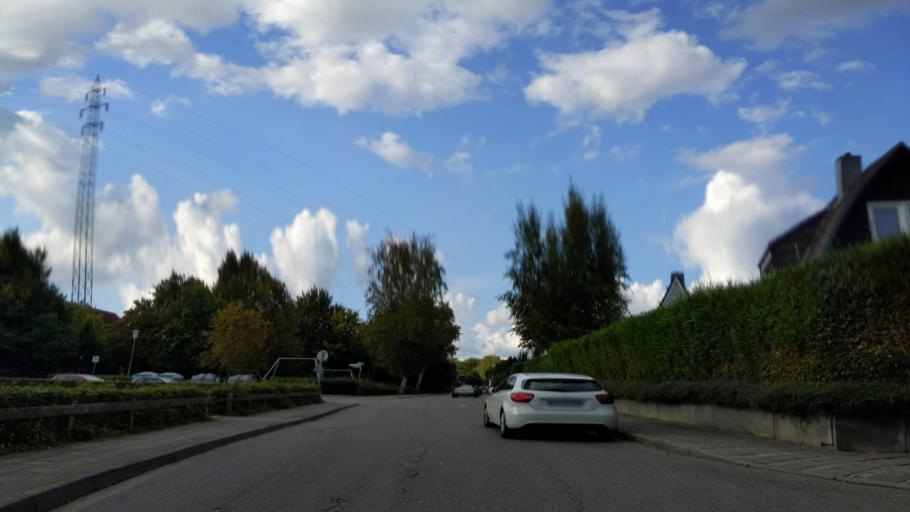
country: DE
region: Schleswig-Holstein
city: Scharbeutz
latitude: 54.0229
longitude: 10.7404
